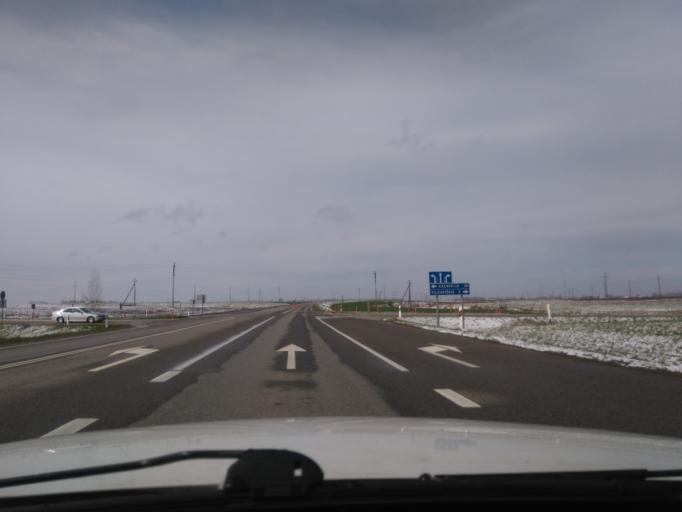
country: LT
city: Vilkaviskis
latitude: 54.6319
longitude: 23.0483
